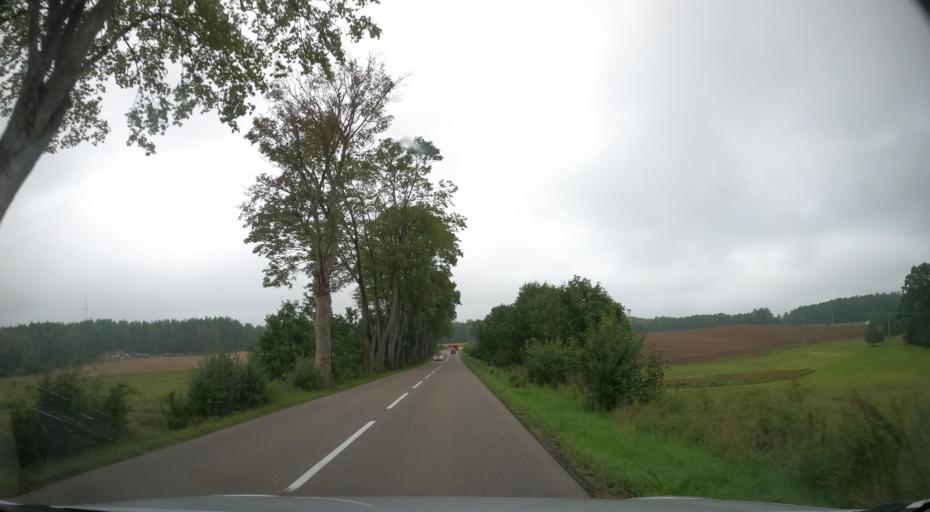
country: PL
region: Pomeranian Voivodeship
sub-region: Powiat wejherowski
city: Linia
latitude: 54.4594
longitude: 18.0407
